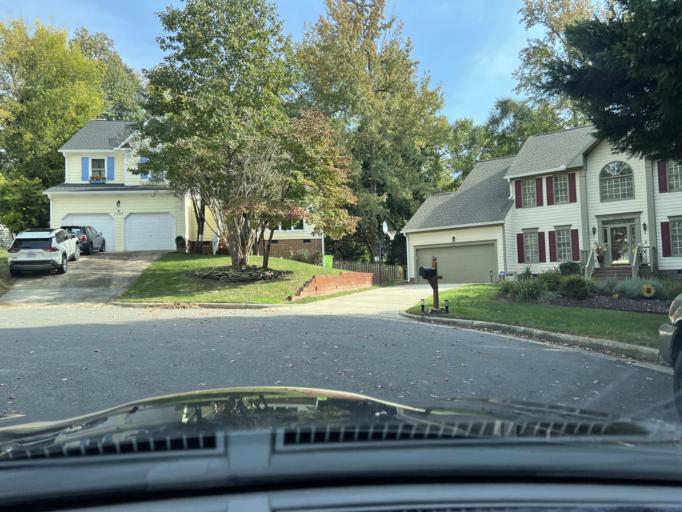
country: US
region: North Carolina
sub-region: Wake County
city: Wake Forest
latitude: 35.9005
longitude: -78.5842
